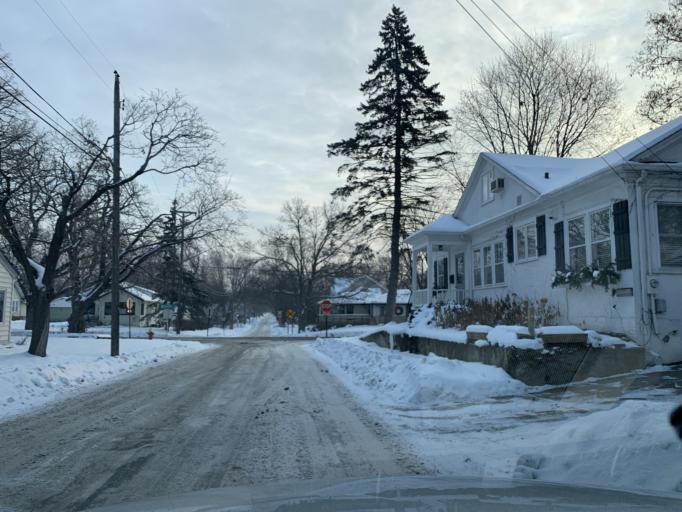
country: US
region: Minnesota
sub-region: Hennepin County
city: Saint Louis Park
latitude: 44.9242
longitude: -93.3563
